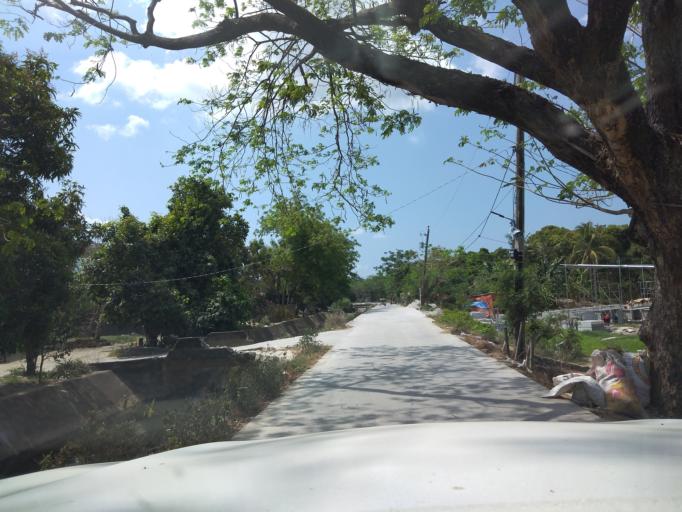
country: PH
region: Central Luzon
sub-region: Province of Pampanga
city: Bahay Pare
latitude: 15.0342
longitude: 120.8754
